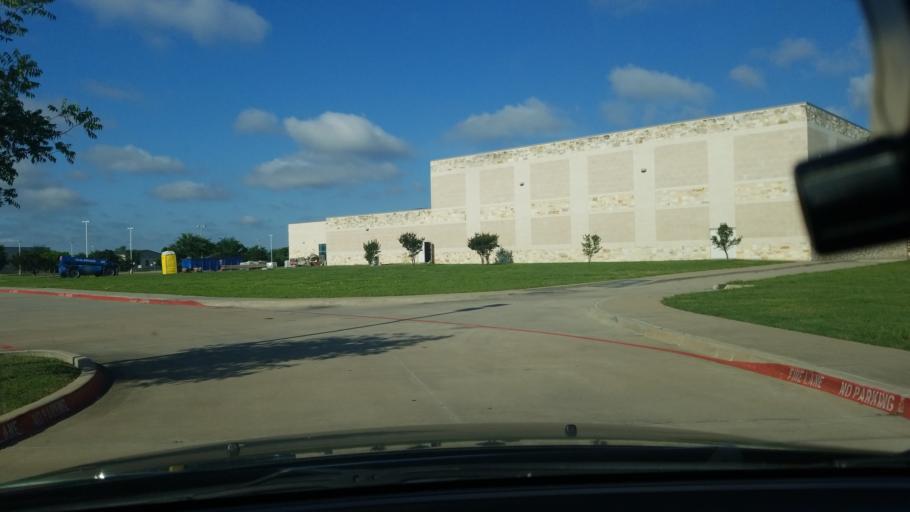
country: US
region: Texas
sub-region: Dallas County
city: Sunnyvale
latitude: 32.7994
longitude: -96.5585
